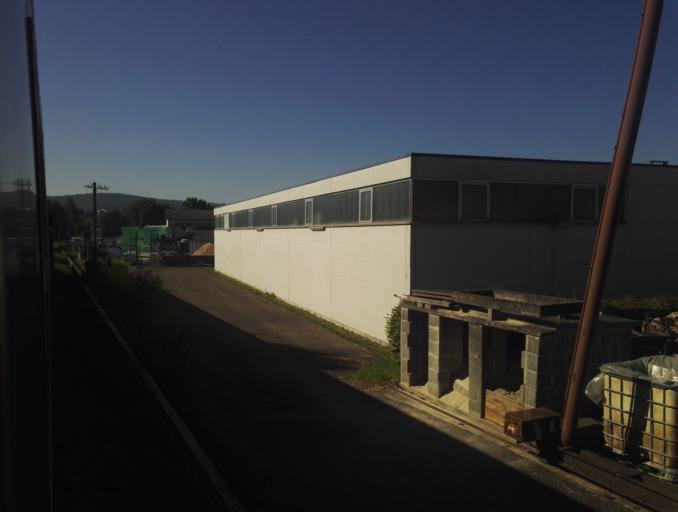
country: DE
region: Baden-Wuerttemberg
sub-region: Regierungsbezirk Stuttgart
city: Urbach
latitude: 48.8240
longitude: 9.5500
